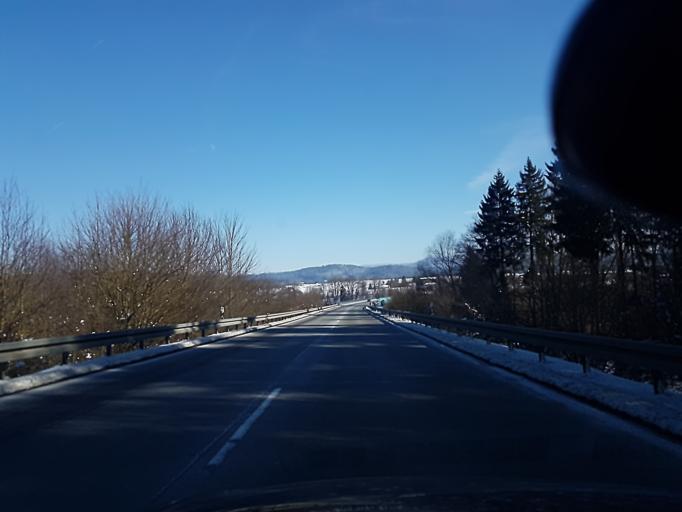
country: DE
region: Baden-Wuerttemberg
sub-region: Freiburg Region
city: Rottweil
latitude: 48.1829
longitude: 8.6244
